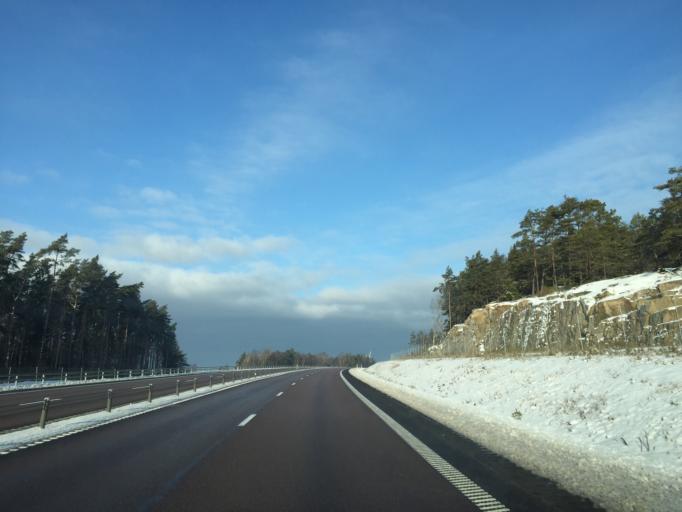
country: SE
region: Vaestra Goetaland
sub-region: Tanums Kommun
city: Tanumshede
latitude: 58.7524
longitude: 11.2868
